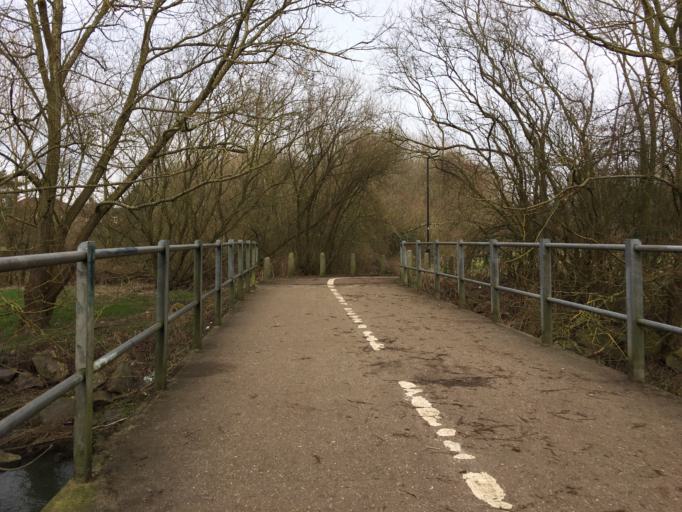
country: GB
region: England
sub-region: Warwickshire
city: Rugby
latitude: 52.3836
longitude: -1.2464
